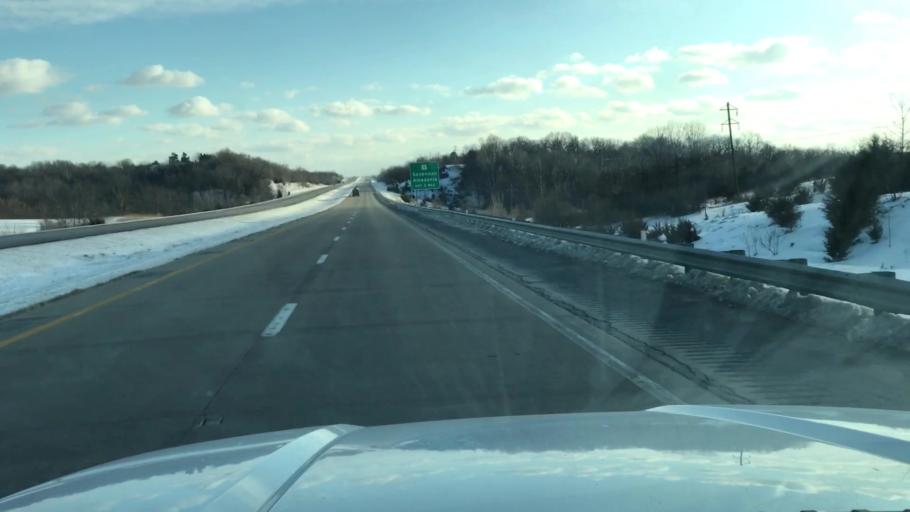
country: US
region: Missouri
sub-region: Andrew County
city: Savannah
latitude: 39.9411
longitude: -94.8603
